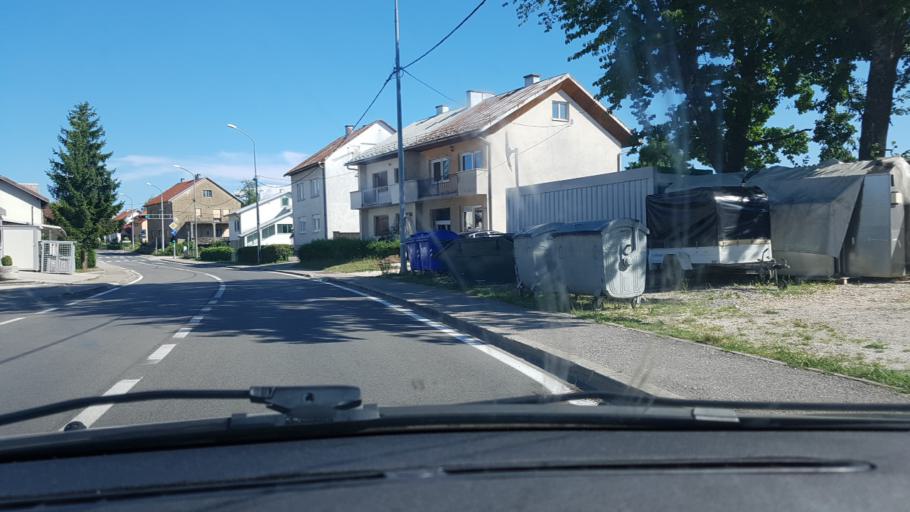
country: HR
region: Licko-Senjska
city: Gospic
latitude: 44.5425
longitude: 15.3744
